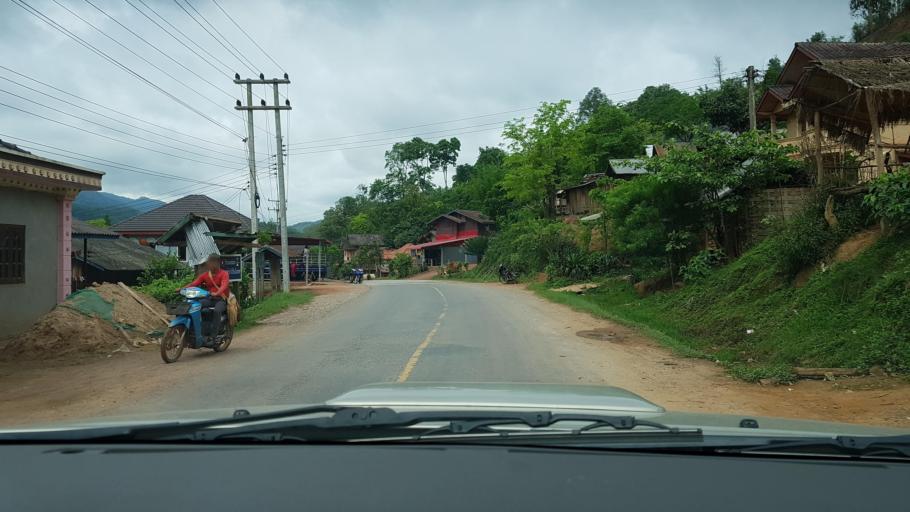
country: LA
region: Oudomxai
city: Muang Xay
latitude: 20.5925
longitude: 101.9343
